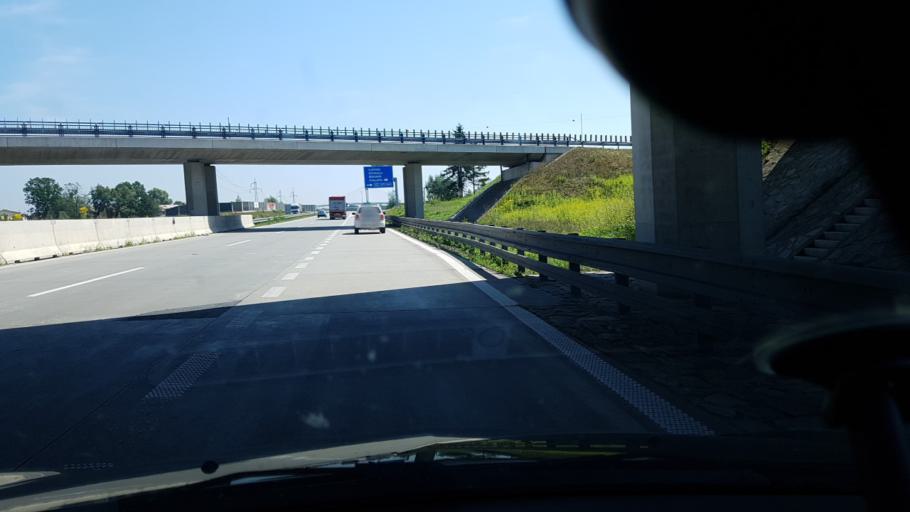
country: CZ
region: Moravskoslezsky
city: Stary Bohumin
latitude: 49.9112
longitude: 18.3298
